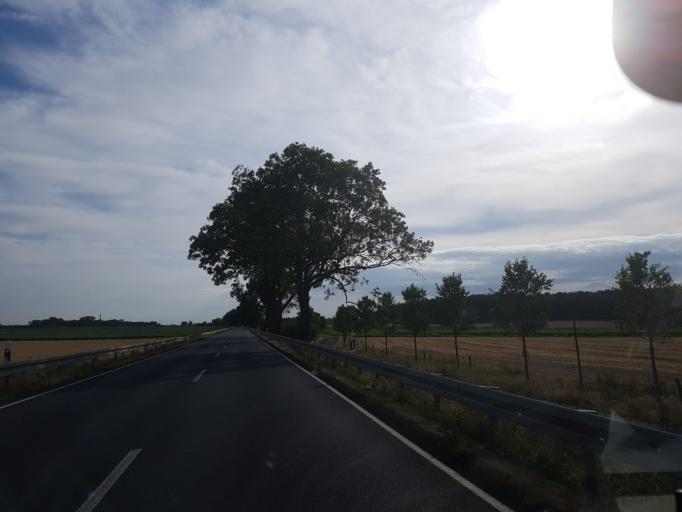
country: DE
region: Brandenburg
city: Schlieben
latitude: 51.7238
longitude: 13.2998
